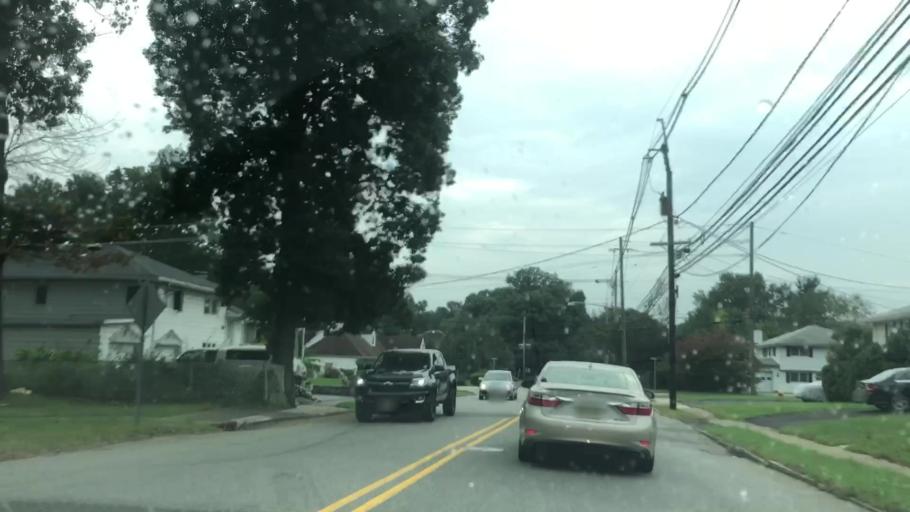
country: US
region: New Jersey
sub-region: Essex County
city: Upper Montclair
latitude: 40.8582
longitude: -74.1888
